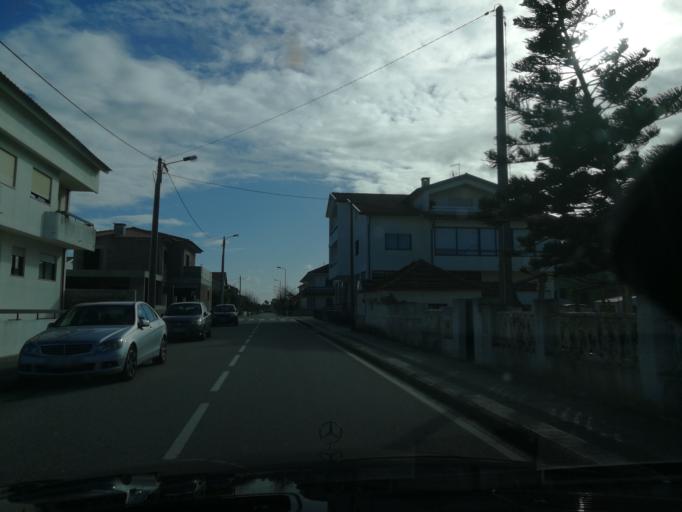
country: PT
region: Aveiro
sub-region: Murtosa
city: Murtosa
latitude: 40.7613
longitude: -8.7086
